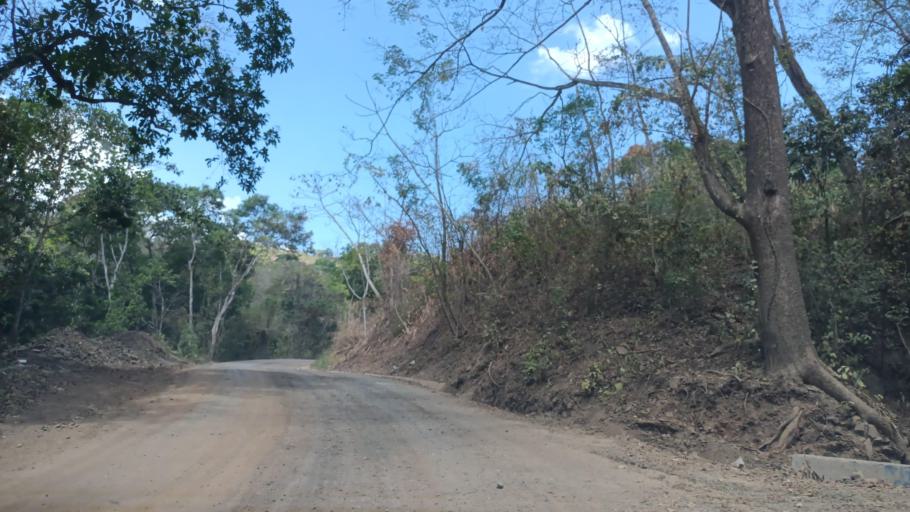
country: PA
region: Panama
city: Las Cumbres
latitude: 9.0719
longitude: -79.5692
